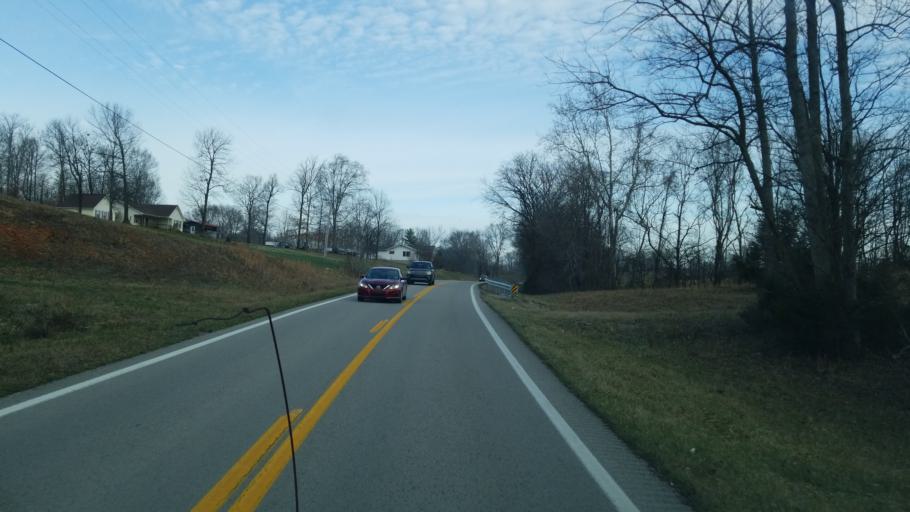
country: US
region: Kentucky
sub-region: Clinton County
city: Albany
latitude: 36.8042
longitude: -85.1811
